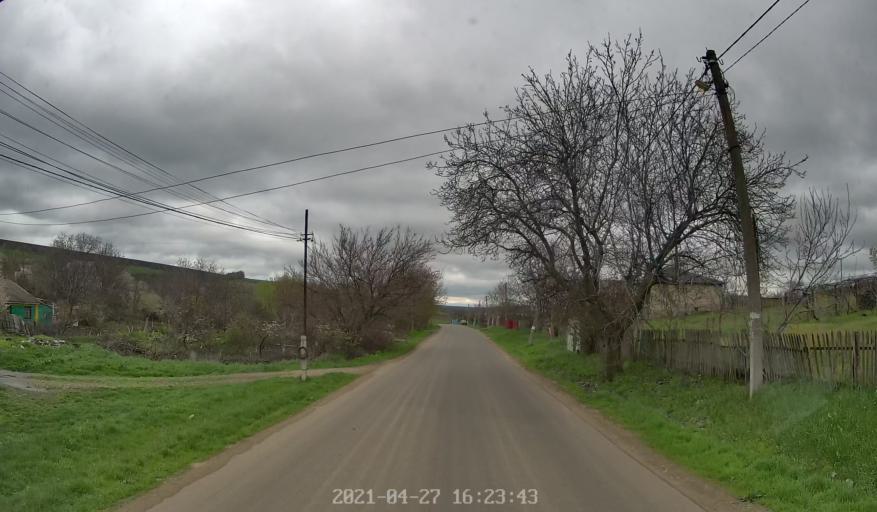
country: MD
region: Chisinau
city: Singera
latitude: 46.9969
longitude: 29.0190
